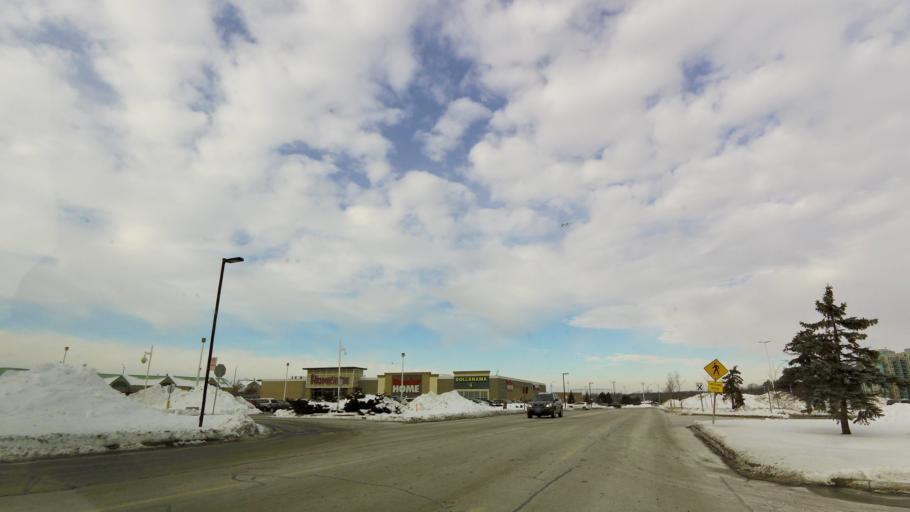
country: CA
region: Ontario
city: Mississauga
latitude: 43.5573
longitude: -79.7146
